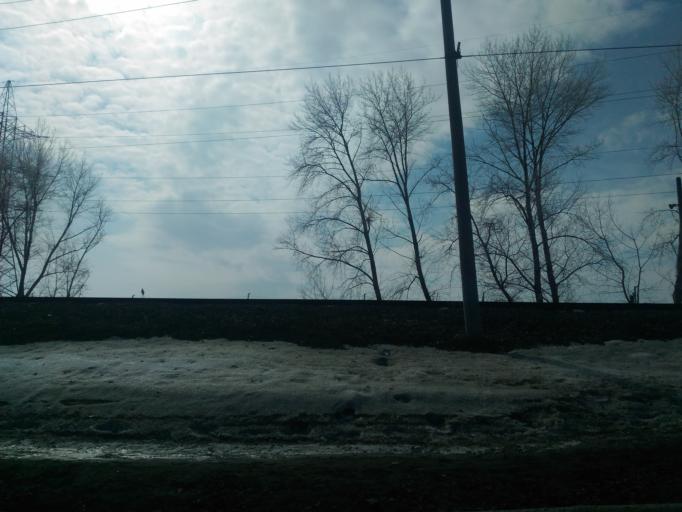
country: RU
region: Ulyanovsk
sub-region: Ulyanovskiy Rayon
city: Ulyanovsk
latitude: 54.3195
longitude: 48.4675
